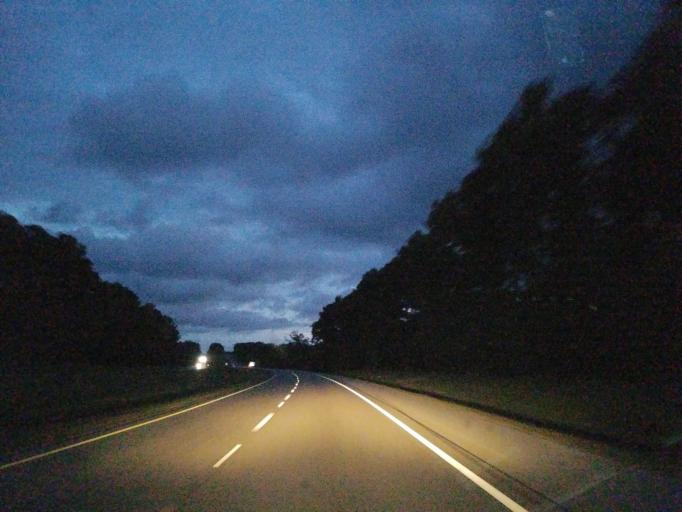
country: US
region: Mississippi
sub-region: Jones County
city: Sharon
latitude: 31.8742
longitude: -89.0452
